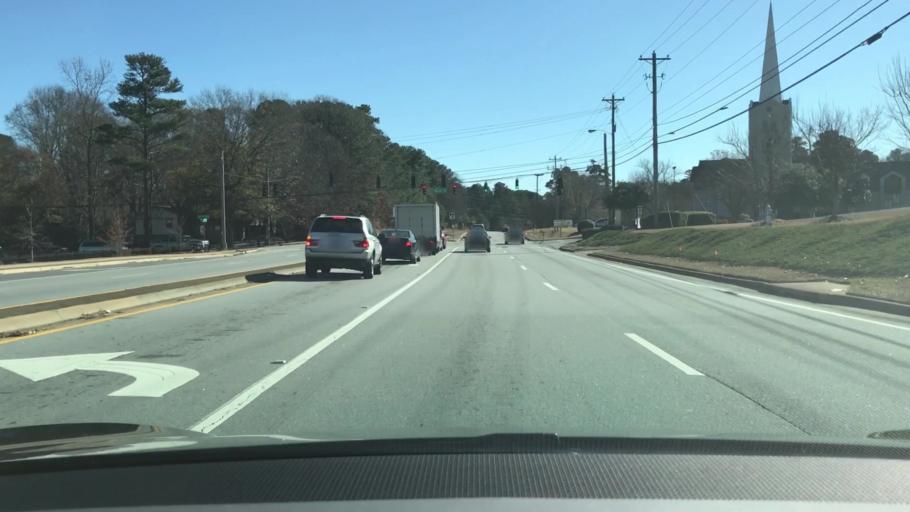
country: US
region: Georgia
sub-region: Gwinnett County
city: Lawrenceville
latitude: 33.9895
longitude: -84.0288
